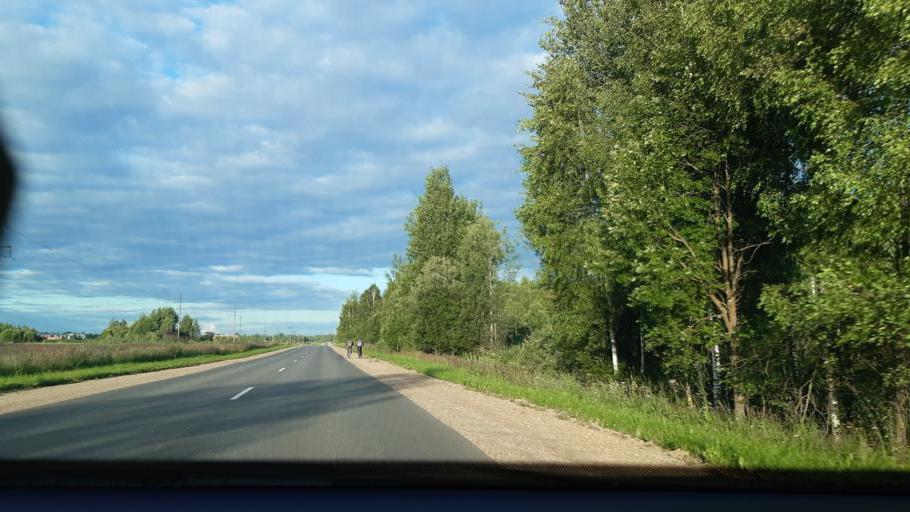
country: RU
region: Smolensk
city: Yel'nya
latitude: 54.5929
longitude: 33.1637
